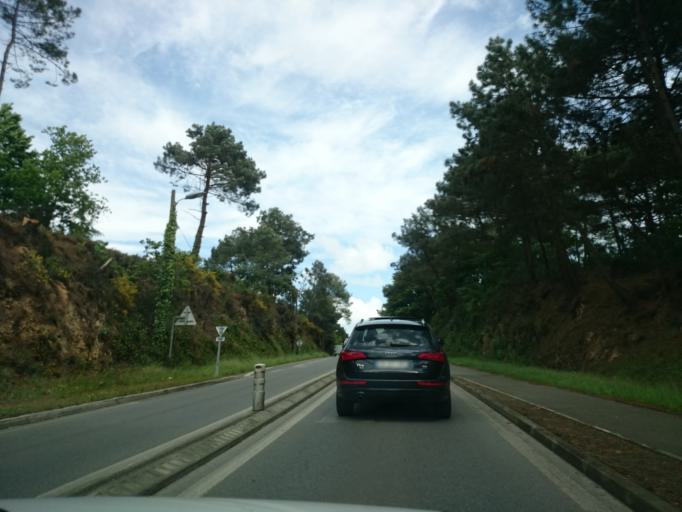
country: FR
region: Brittany
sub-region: Departement du Morbihan
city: Arradon
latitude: 47.6496
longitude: -2.7956
